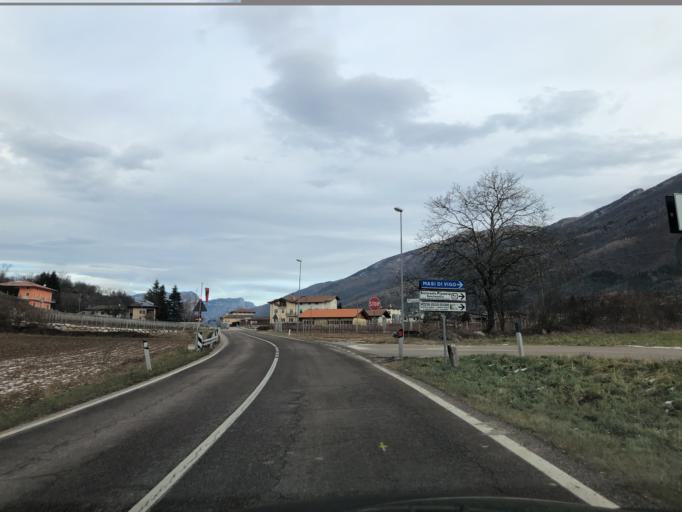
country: IT
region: Trentino-Alto Adige
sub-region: Provincia di Trento
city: Cavedine
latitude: 45.9725
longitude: 10.9740
